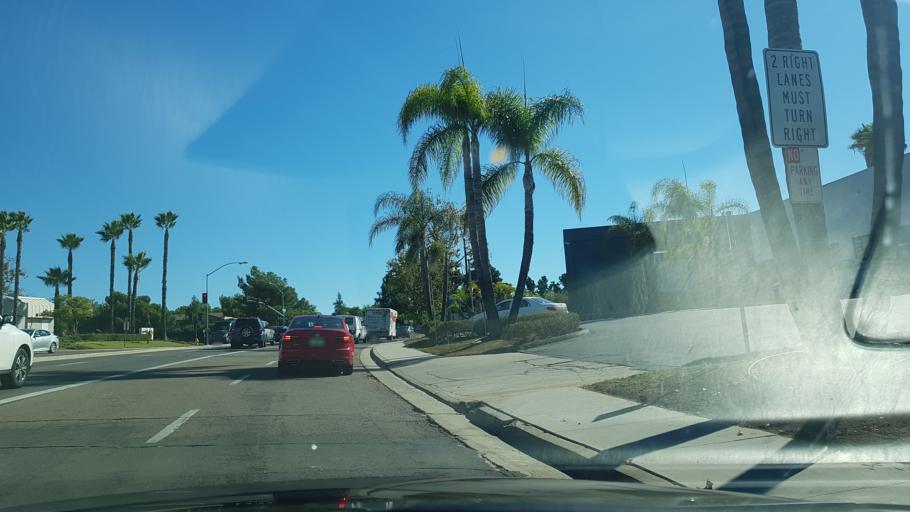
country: US
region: California
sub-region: San Diego County
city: Fairbanks Ranch
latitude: 32.8947
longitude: -117.1340
